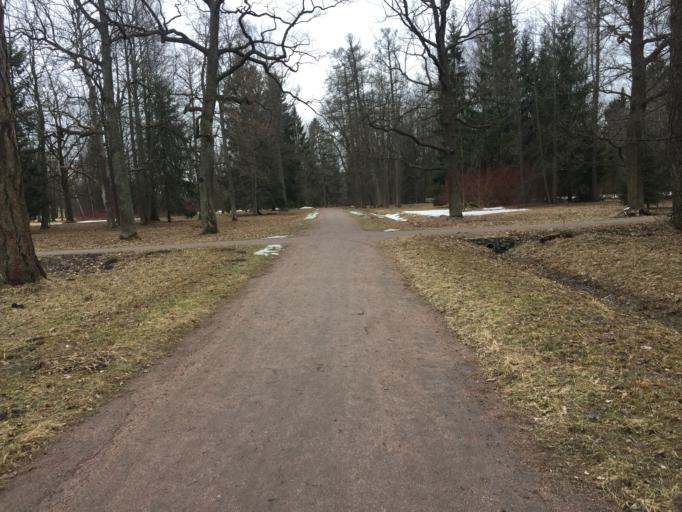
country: RU
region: St.-Petersburg
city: Pushkin
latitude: 59.7215
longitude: 30.3842
